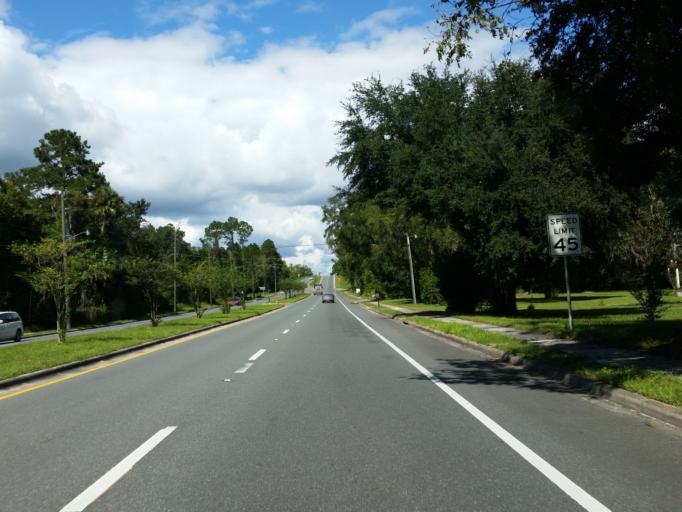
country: US
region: Florida
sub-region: Alachua County
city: Waldo
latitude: 29.7846
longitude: -82.1674
